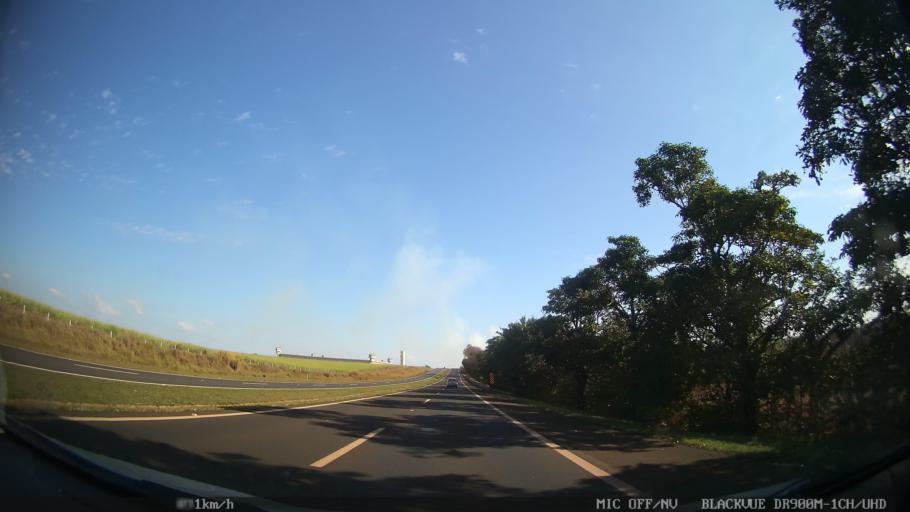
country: BR
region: Sao Paulo
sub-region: Piracicaba
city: Piracicaba
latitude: -22.6746
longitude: -47.5600
